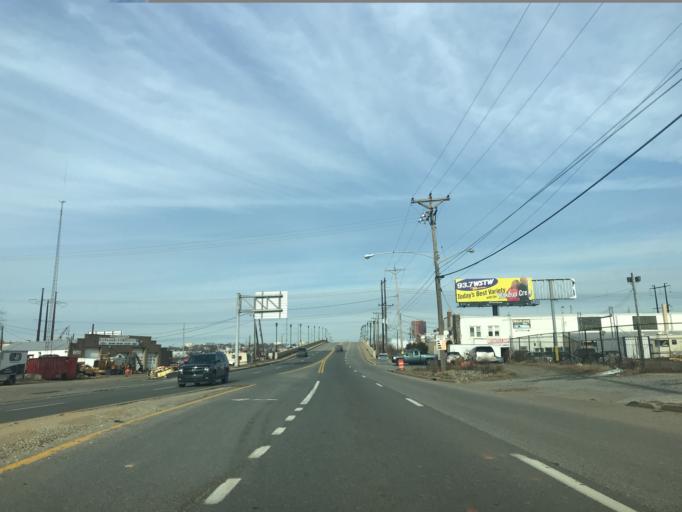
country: US
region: Delaware
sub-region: New Castle County
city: Wilmington
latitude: 39.7219
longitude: -75.5556
